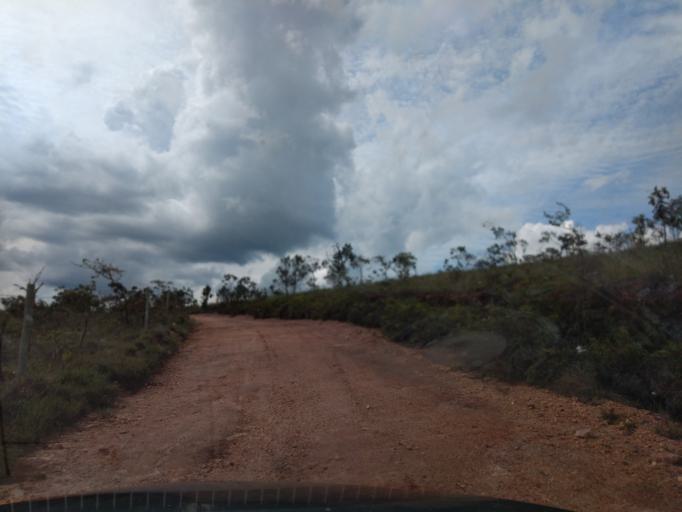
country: BR
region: Minas Gerais
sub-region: Lavras
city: Lavras
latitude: -21.5294
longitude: -44.8902
